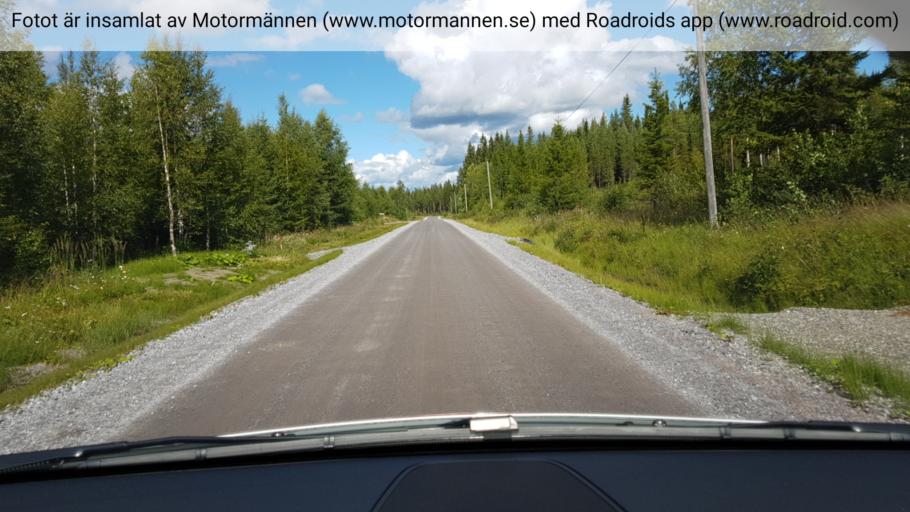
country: SE
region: Jaemtland
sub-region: Braecke Kommun
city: Braecke
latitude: 63.1092
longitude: 15.7467
